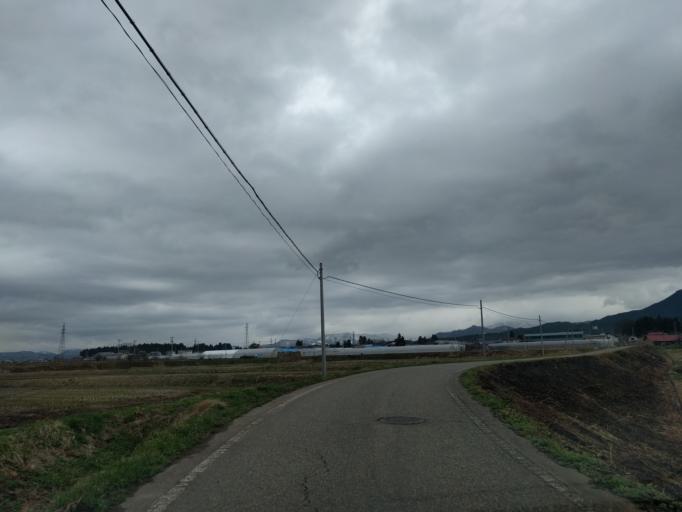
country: JP
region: Fukushima
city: Kitakata
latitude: 37.6536
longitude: 139.9168
